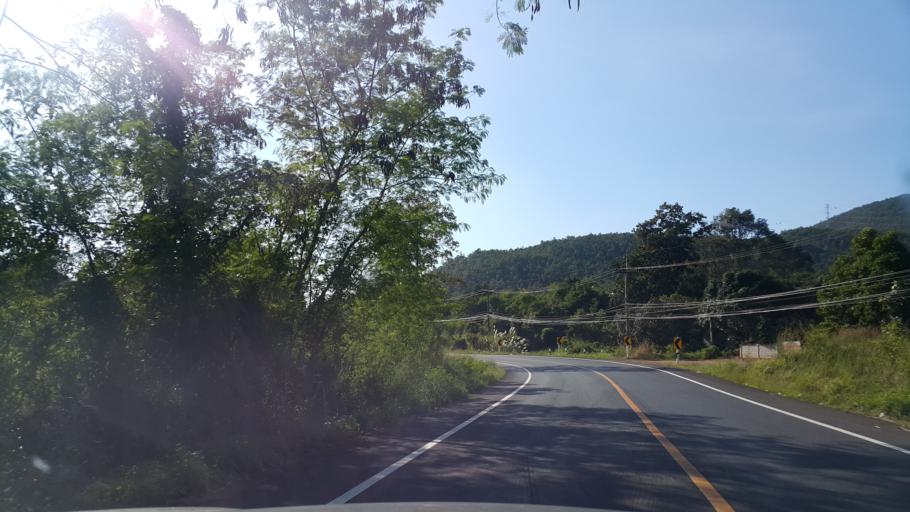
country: TH
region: Lamphun
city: Mae Tha
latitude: 18.4684
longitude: 99.1528
